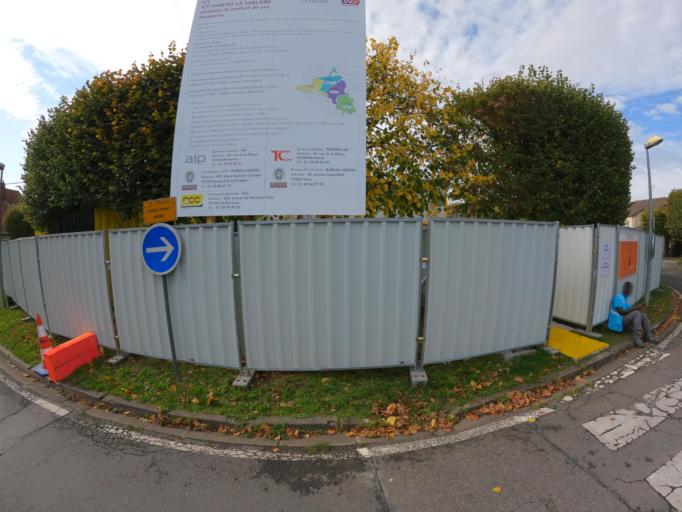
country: FR
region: Ile-de-France
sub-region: Departement de Seine-et-Marne
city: Brou-sur-Chantereine
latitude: 48.8843
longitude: 2.6209
